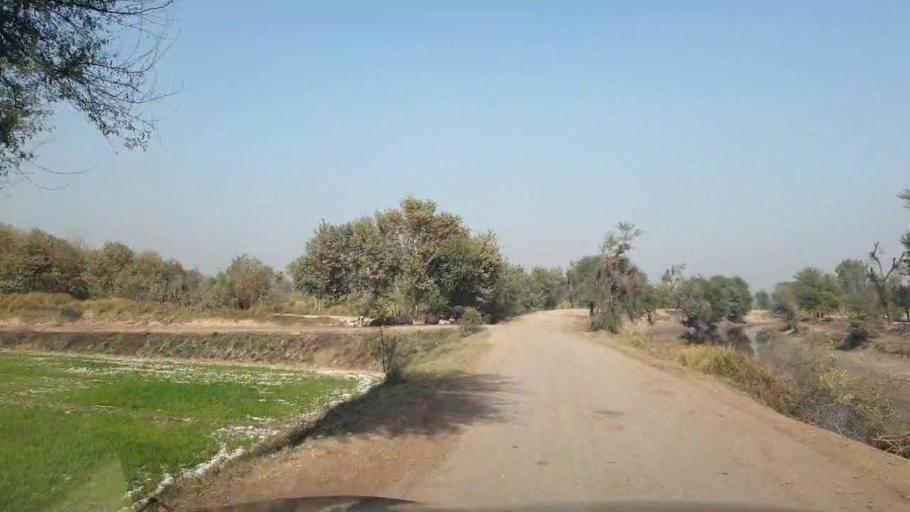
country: PK
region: Sindh
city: Ubauro
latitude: 28.1374
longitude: 69.7722
